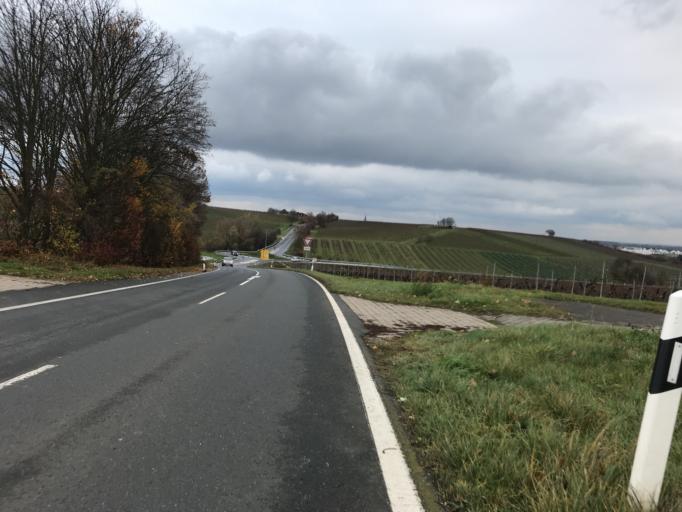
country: DE
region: Rheinland-Pfalz
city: Gau-Bischofsheim
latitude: 49.9178
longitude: 8.2914
